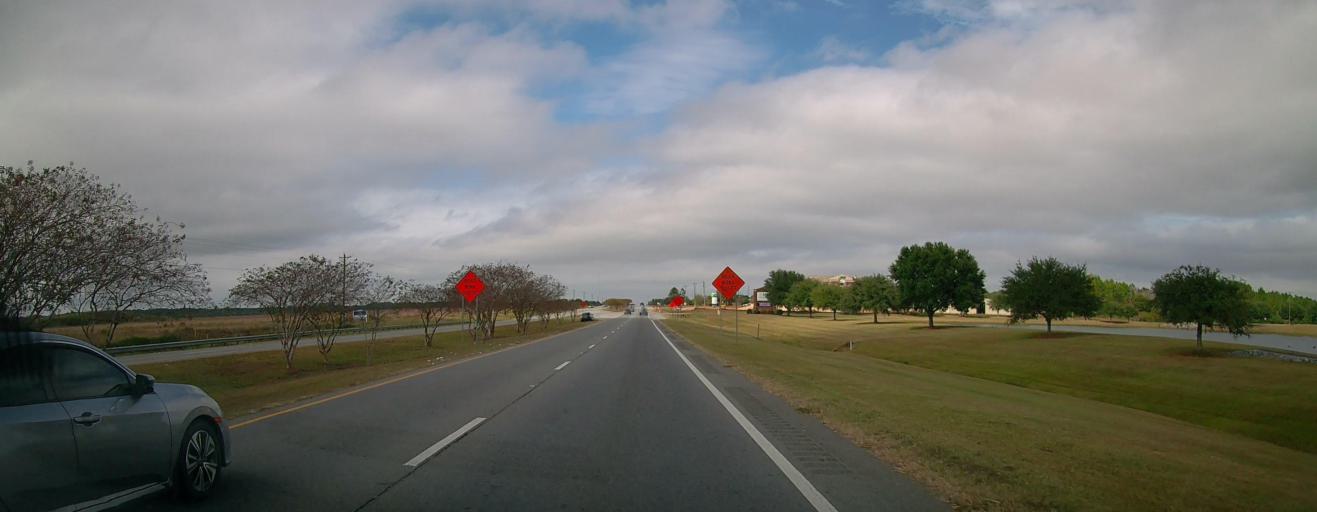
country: US
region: Georgia
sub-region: Colquitt County
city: Moultrie
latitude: 31.1958
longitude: -83.7671
